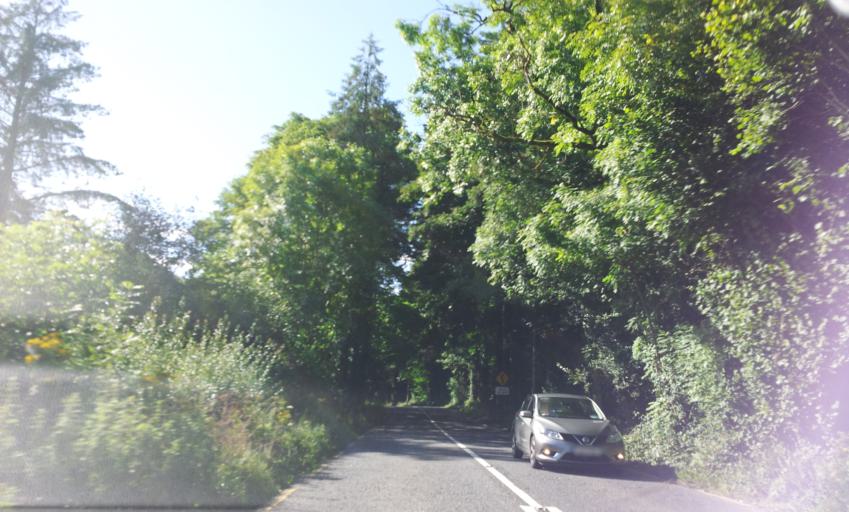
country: IE
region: Munster
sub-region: County Cork
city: Millstreet
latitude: 51.9250
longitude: -9.1012
